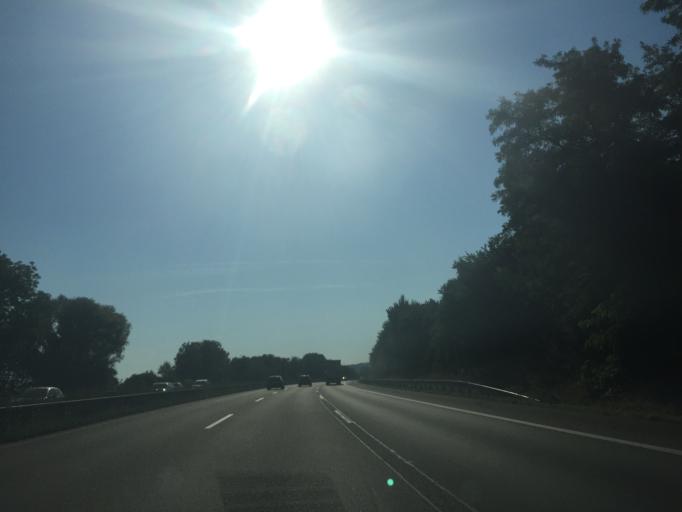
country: DE
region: Baden-Wuerttemberg
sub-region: Karlsruhe Region
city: Dielheim
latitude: 49.2805
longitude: 8.7212
